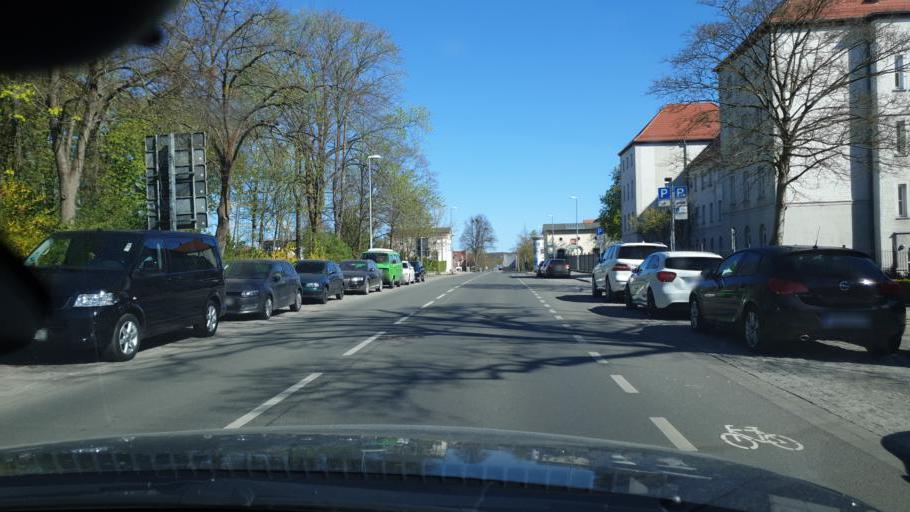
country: DE
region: Mecklenburg-Vorpommern
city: Werdervorstadt
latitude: 53.6387
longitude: 11.4238
